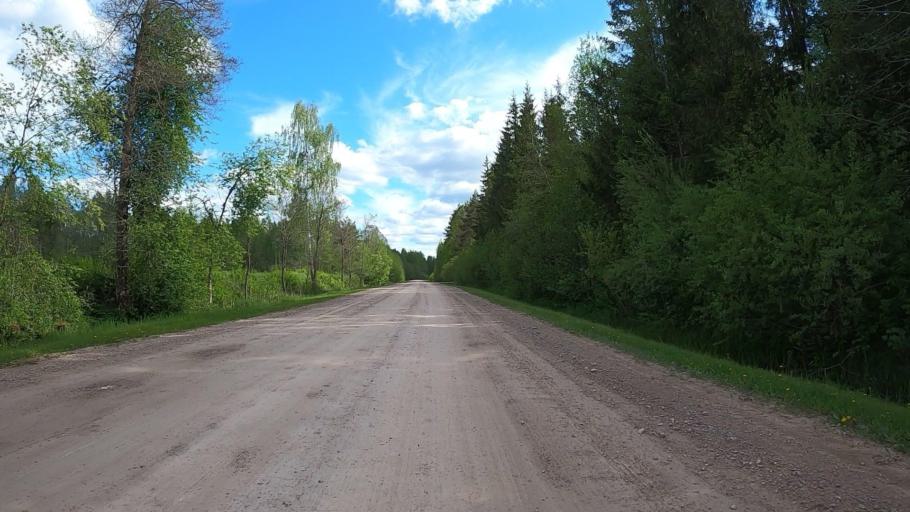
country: LV
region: Jurmala
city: Jurmala
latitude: 56.8636
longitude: 23.7876
